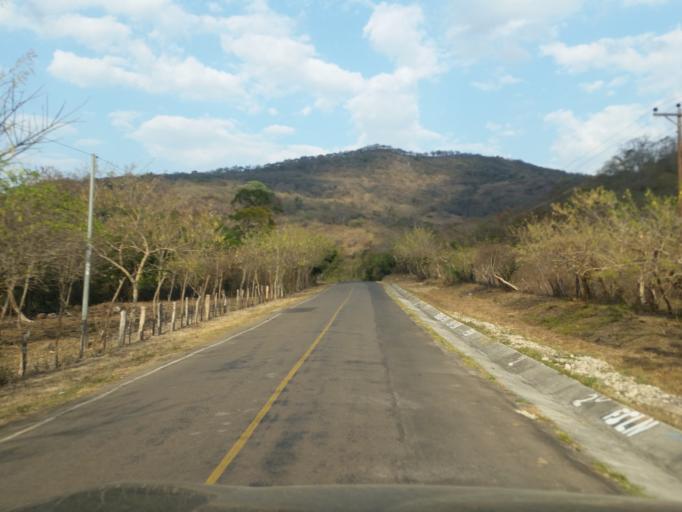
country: NI
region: Jinotega
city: La Concordia
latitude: 13.1924
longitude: -86.1418
